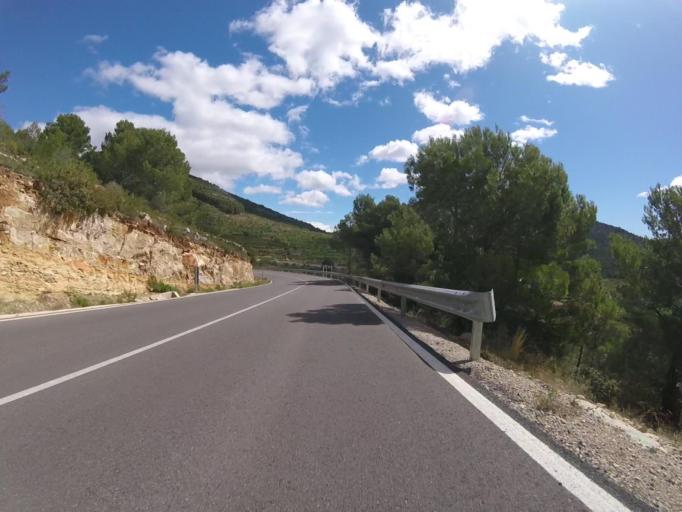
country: ES
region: Valencia
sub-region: Provincia de Castello
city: Culla
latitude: 40.2943
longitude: -0.1148
